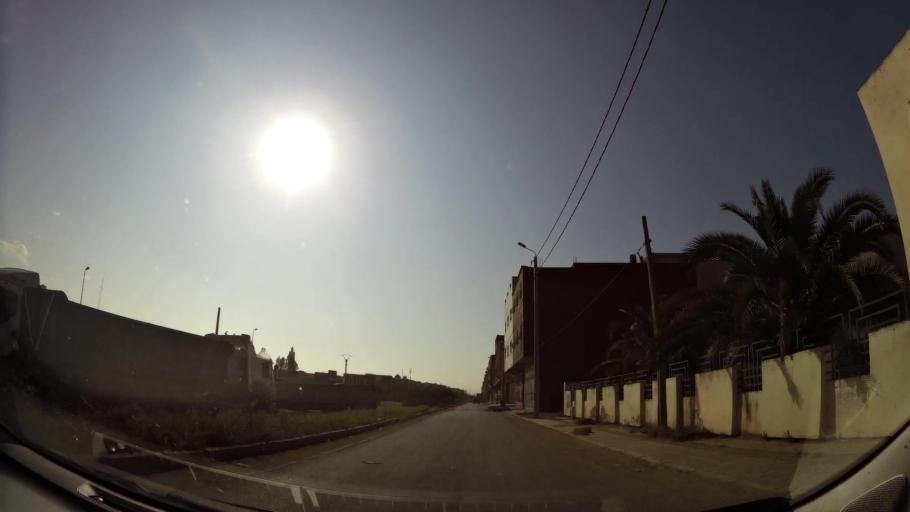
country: MA
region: Oriental
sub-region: Oujda-Angad
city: Oujda
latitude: 34.6804
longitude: -1.9419
